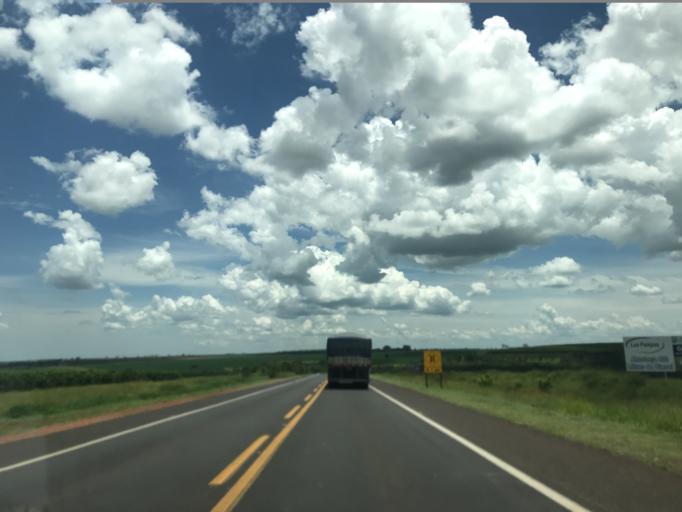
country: BR
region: Minas Gerais
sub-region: Prata
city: Prata
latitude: -19.5270
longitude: -48.8317
